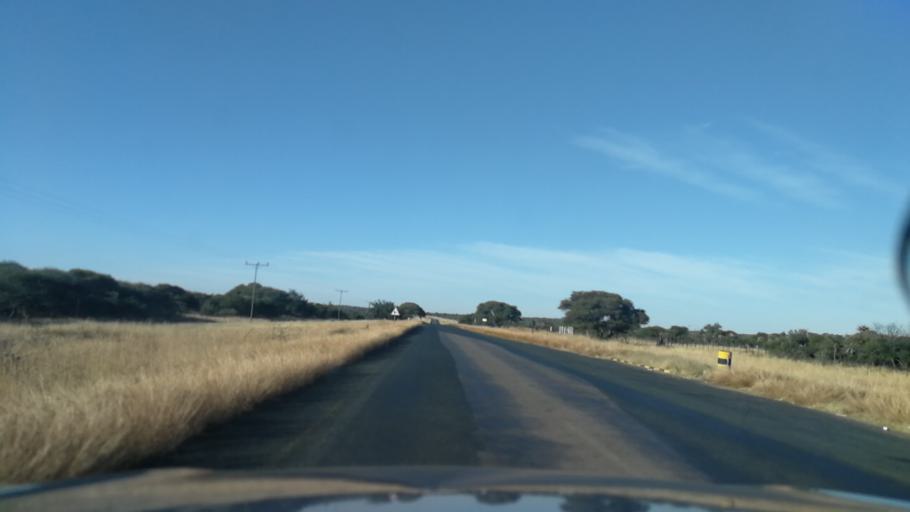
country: BW
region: South East
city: Lobatse
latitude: -25.3137
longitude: 25.6157
